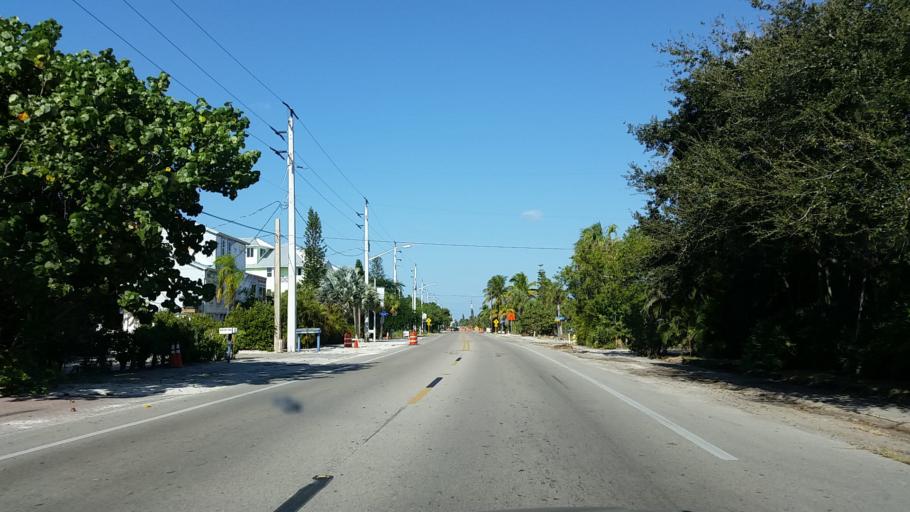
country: US
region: Florida
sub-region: Lee County
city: Fort Myers Beach
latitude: 26.4387
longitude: -81.9240
